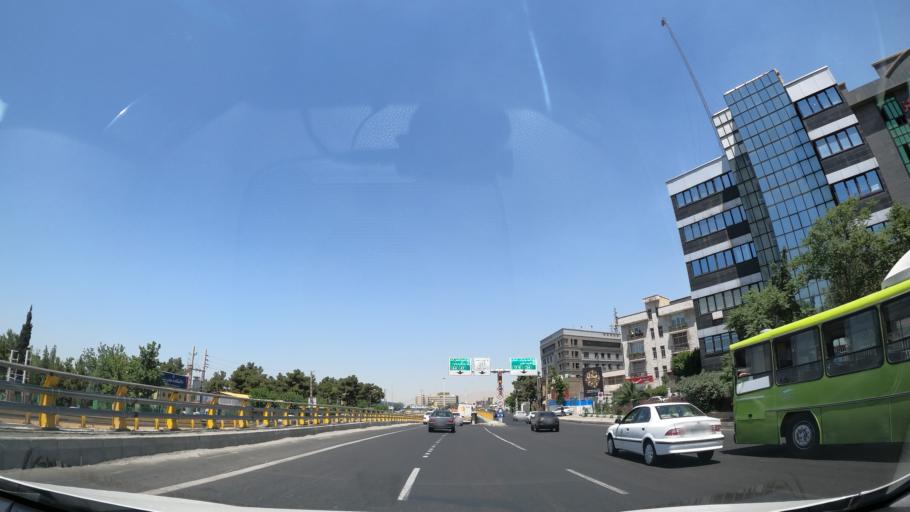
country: IR
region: Tehran
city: Tehran
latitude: 35.7241
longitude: 51.3839
